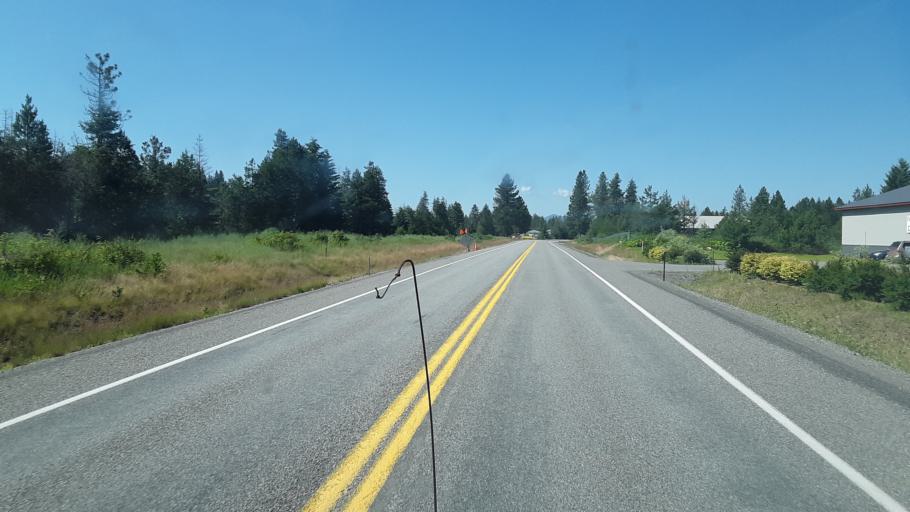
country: US
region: Idaho
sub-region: Kootenai County
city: Hayden
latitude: 47.8282
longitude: -116.7826
